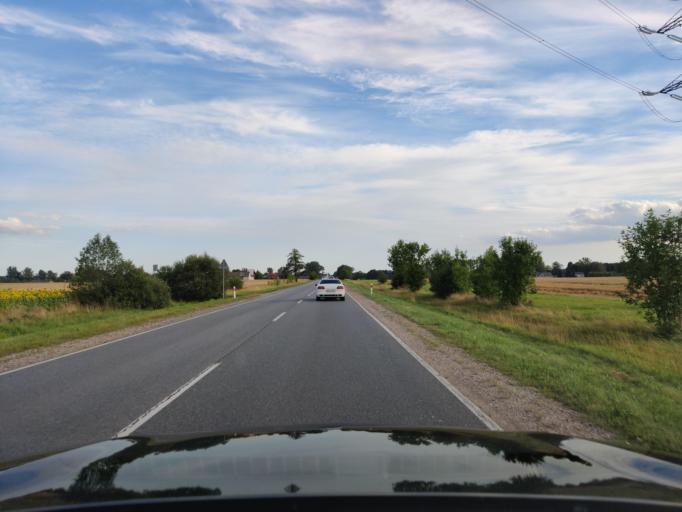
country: PL
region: Masovian Voivodeship
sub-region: Powiat minski
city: Stanislawow
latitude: 52.2676
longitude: 21.5491
